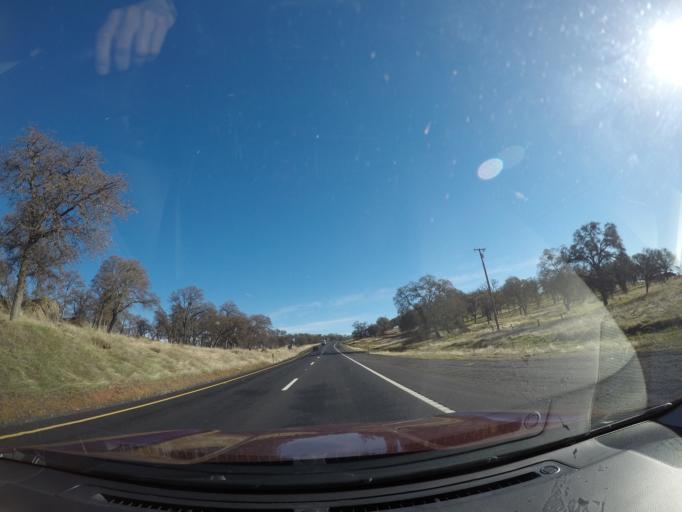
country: US
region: California
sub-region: Calaveras County
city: Copperopolis
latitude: 37.8500
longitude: -120.5927
